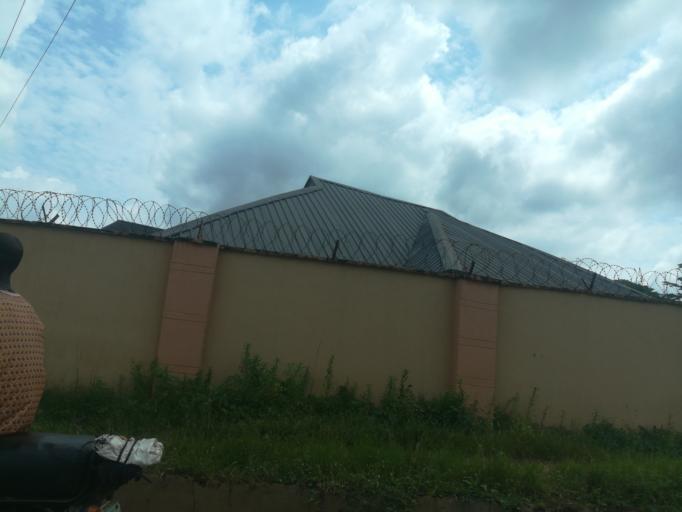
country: NG
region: Oyo
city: Ibadan
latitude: 7.3678
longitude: 3.8231
